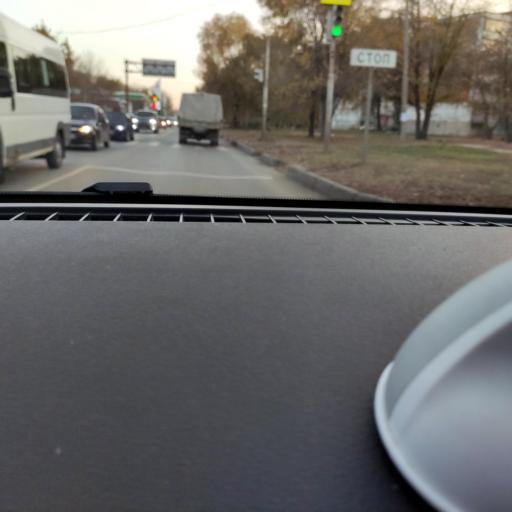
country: RU
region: Samara
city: Petra-Dubrava
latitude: 53.2477
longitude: 50.2680
